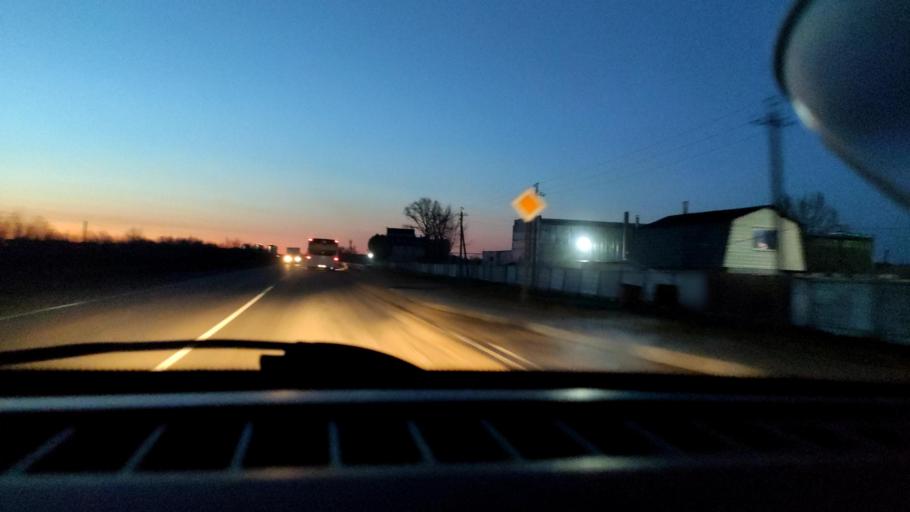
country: RU
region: Samara
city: Samara
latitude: 53.1279
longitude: 50.1110
